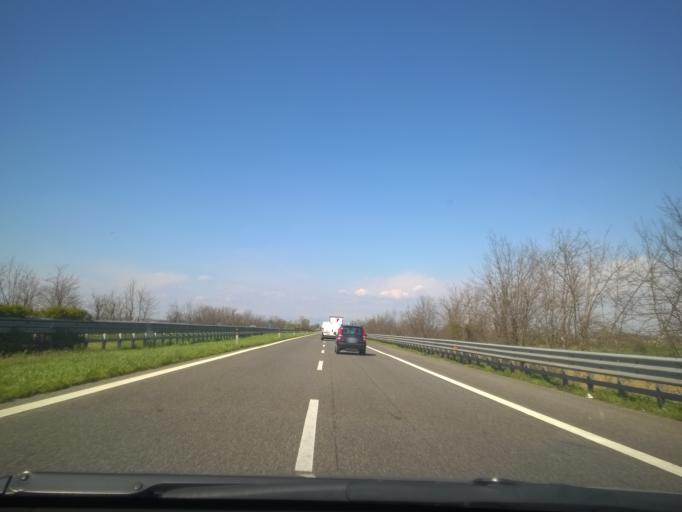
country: IT
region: Lombardy
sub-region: Provincia di Brescia
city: Alfianello
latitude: 45.2491
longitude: 10.1220
